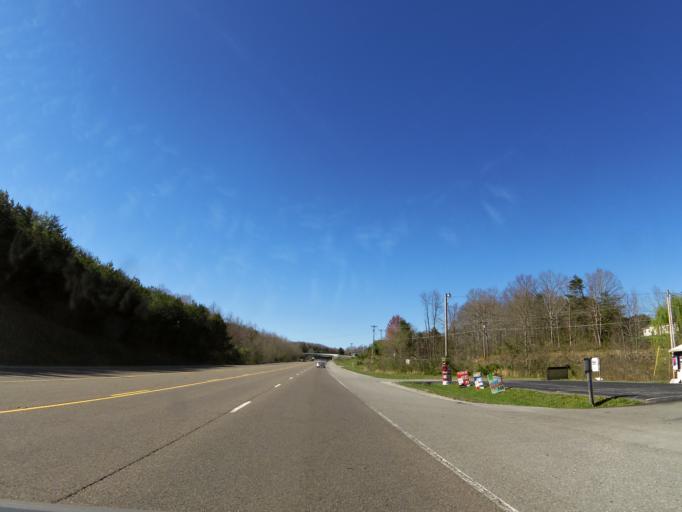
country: US
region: Tennessee
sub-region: Scott County
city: Oneida
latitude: 36.4529
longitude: -84.5447
